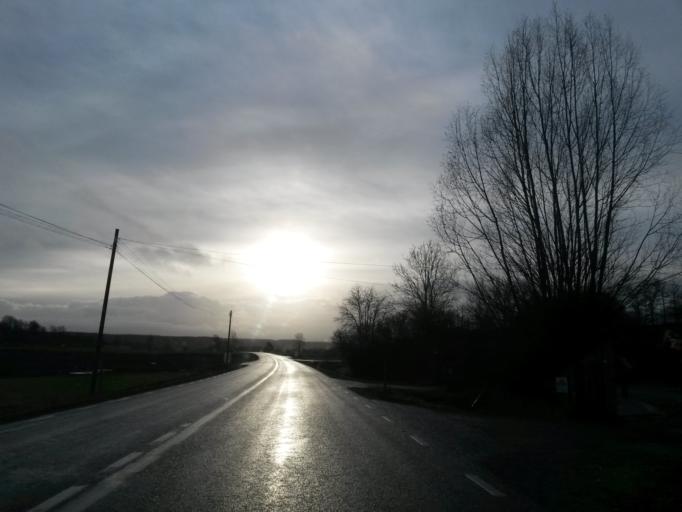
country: SE
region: Vaestra Goetaland
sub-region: Harryda Kommun
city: Ravlanda
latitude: 57.5343
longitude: 12.5323
